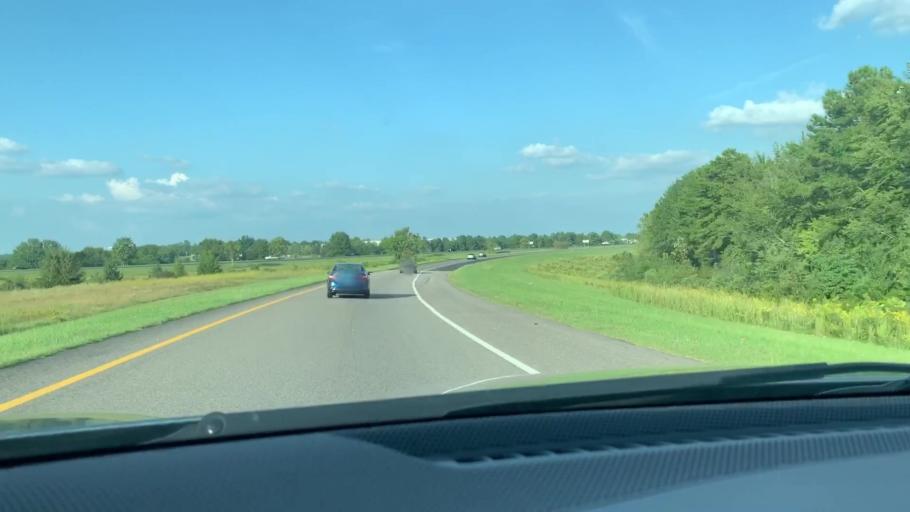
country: US
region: South Carolina
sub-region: Lexington County
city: Cayce
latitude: 33.9256
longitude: -81.0667
